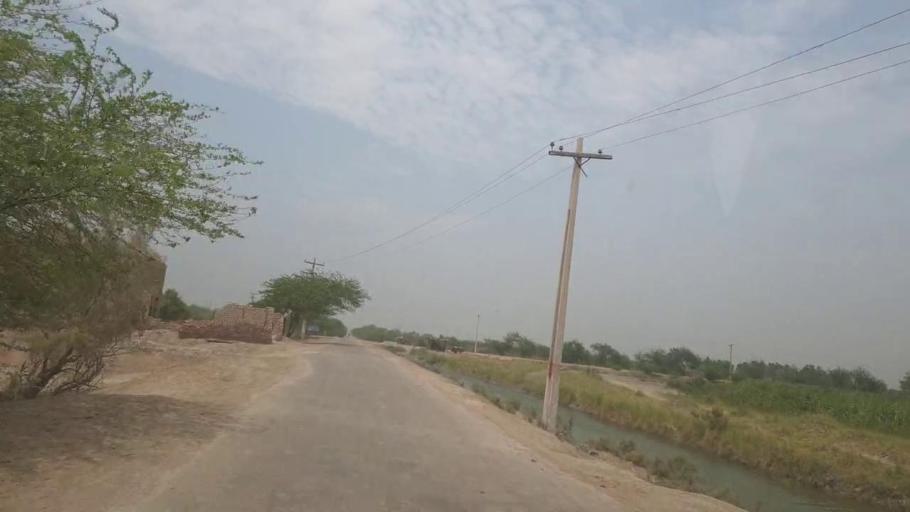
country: PK
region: Sindh
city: Kot Diji
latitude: 27.4359
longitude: 68.7115
